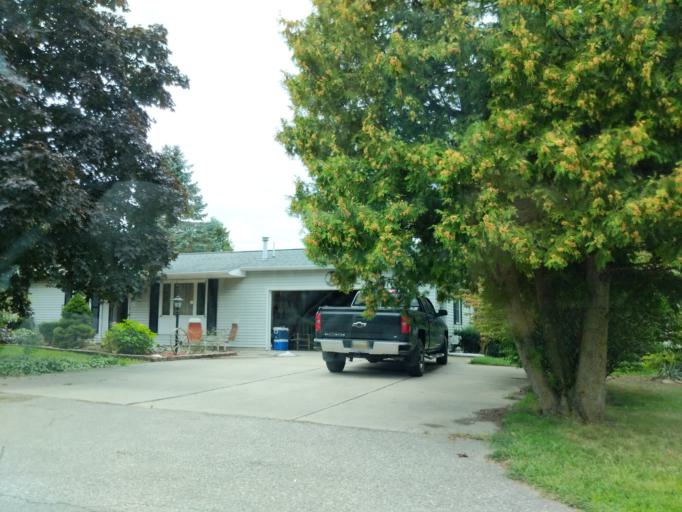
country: US
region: Michigan
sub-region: Lapeer County
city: Barnes Lake-Millers Lake
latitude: 43.3346
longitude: -83.3570
